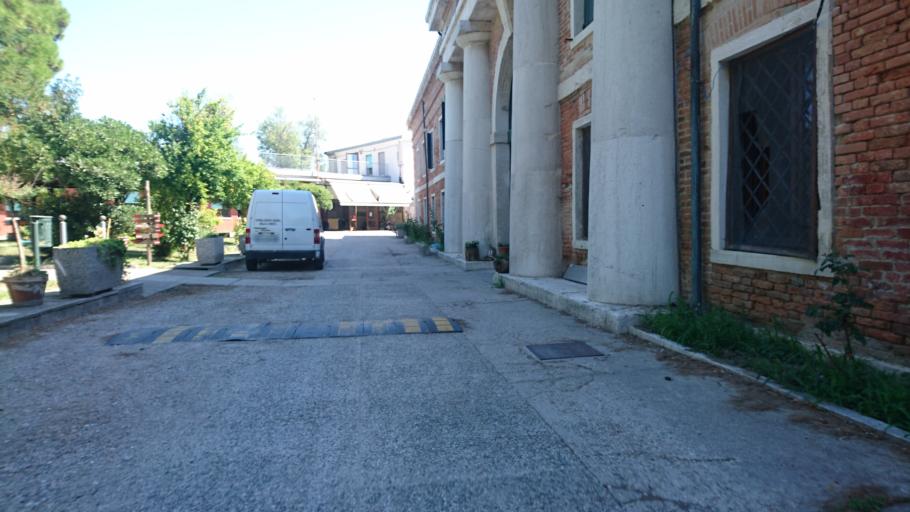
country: IT
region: Veneto
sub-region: Provincia di Venezia
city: San Pietro in Volta
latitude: 45.3334
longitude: 12.3187
